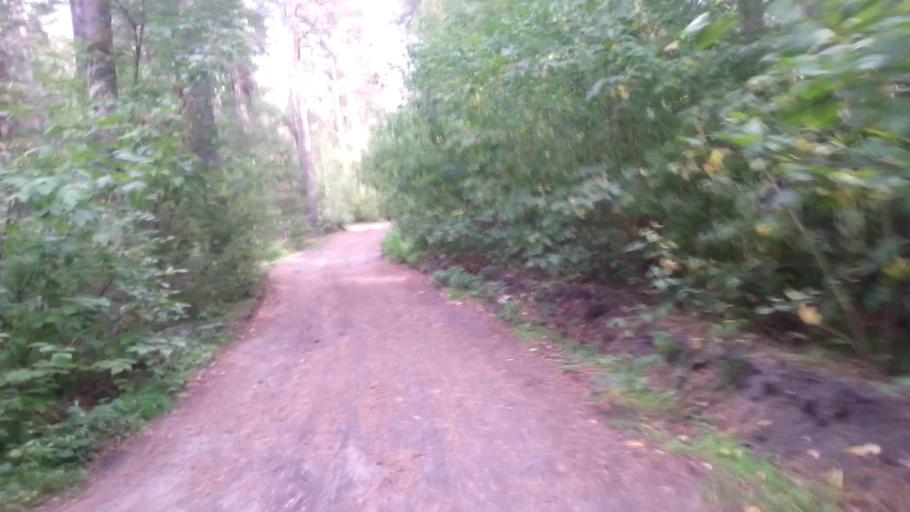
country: RU
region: Altai Krai
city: Yuzhnyy
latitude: 53.3100
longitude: 83.6946
